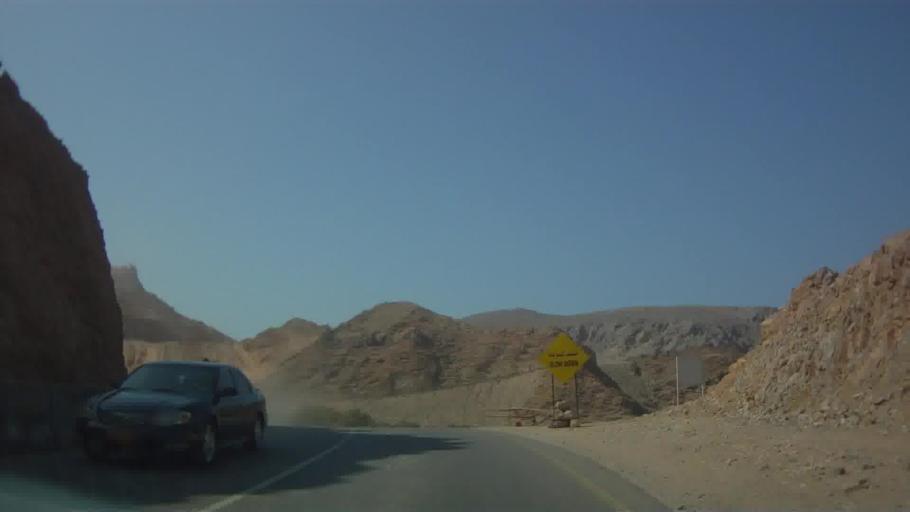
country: OM
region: Muhafazat Masqat
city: Muscat
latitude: 23.5095
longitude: 58.7240
